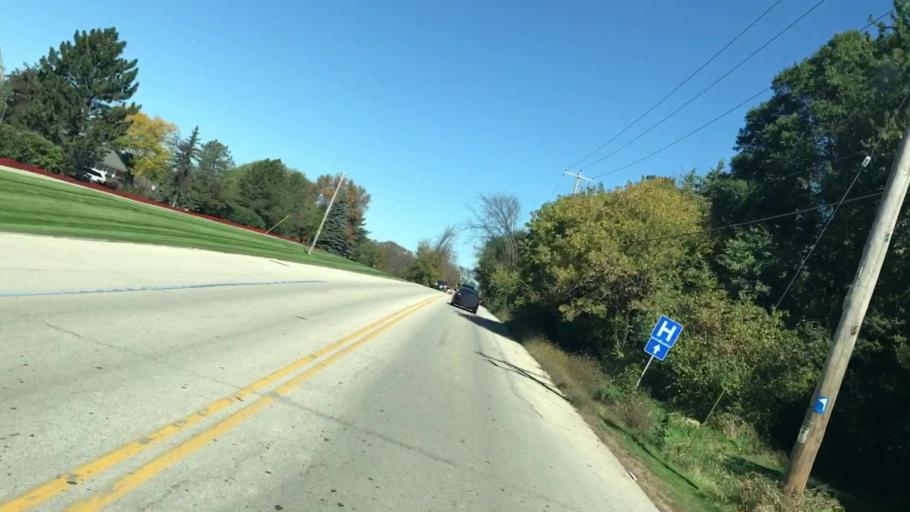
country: US
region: Wisconsin
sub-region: Waukesha County
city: Brookfield
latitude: 43.0542
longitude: -88.1664
